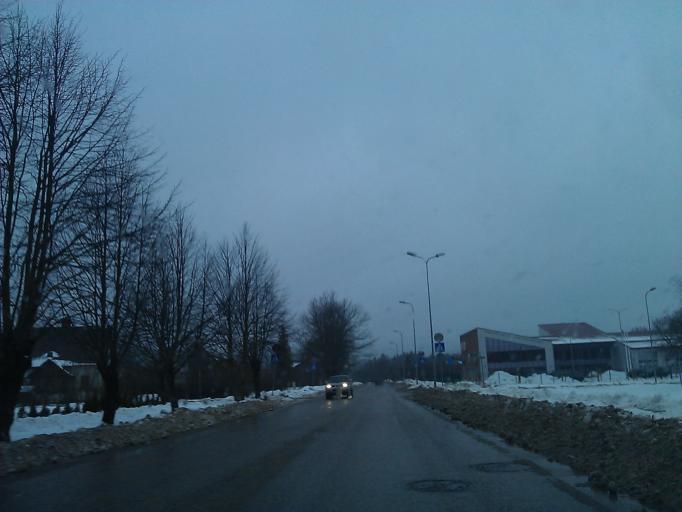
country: LV
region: Cesu Rajons
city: Cesis
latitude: 57.3048
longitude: 25.2886
